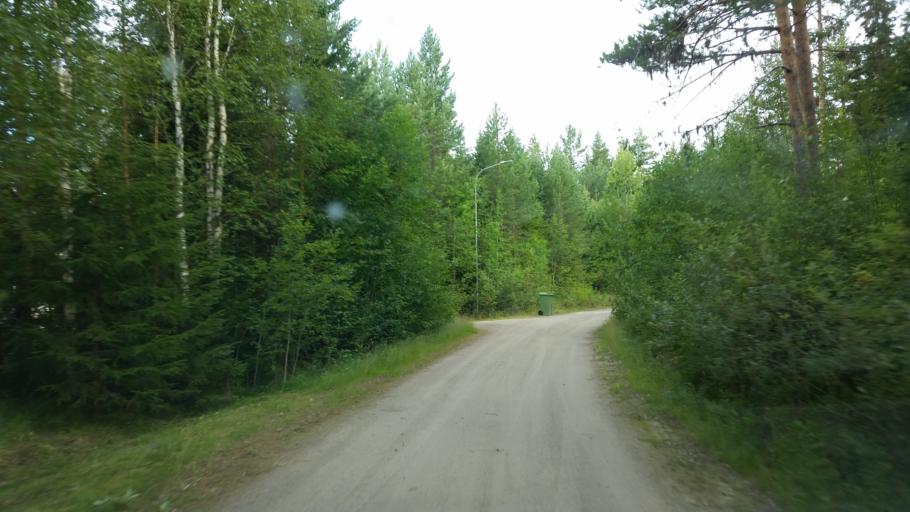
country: SE
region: Vaesternorrland
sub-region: Ange Kommun
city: Ange
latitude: 62.1881
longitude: 15.6441
